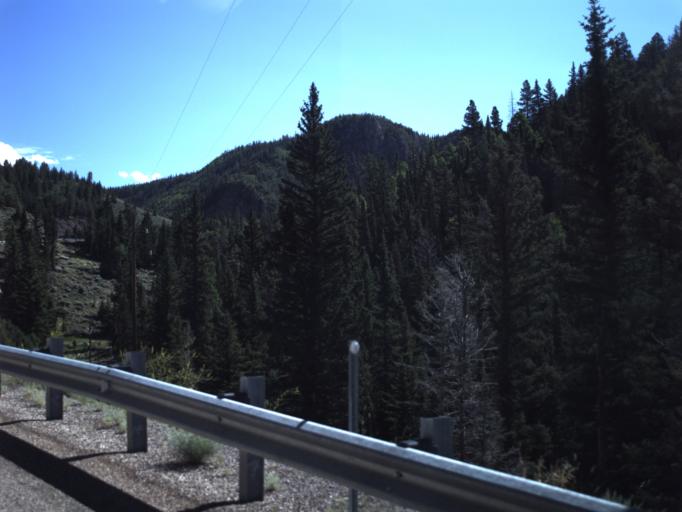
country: US
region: Utah
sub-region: Beaver County
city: Beaver
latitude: 38.2783
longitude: -112.4584
